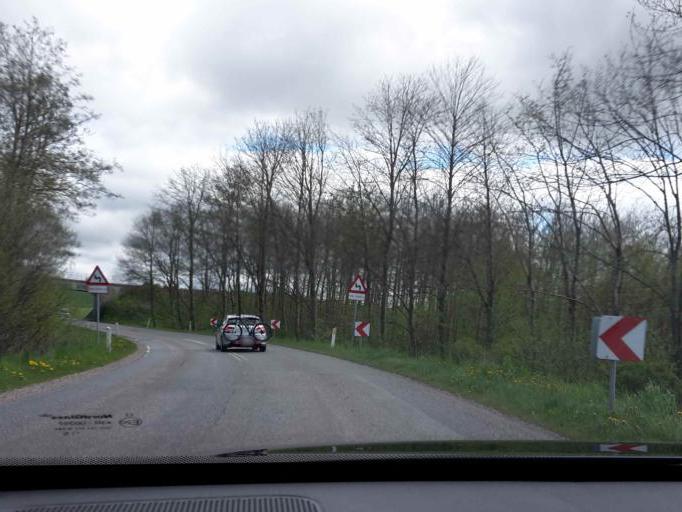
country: DK
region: Central Jutland
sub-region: Syddjurs Kommune
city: Hornslet
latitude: 56.3444
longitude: 10.3439
